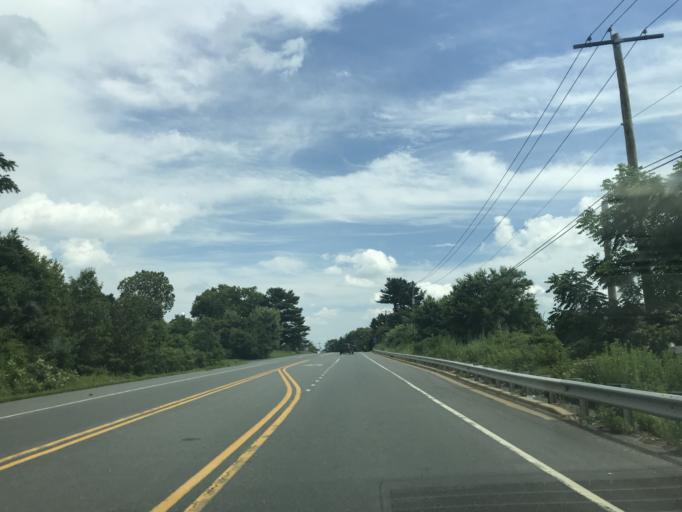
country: US
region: Delaware
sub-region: New Castle County
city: Hockessin
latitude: 39.7674
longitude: -75.6565
